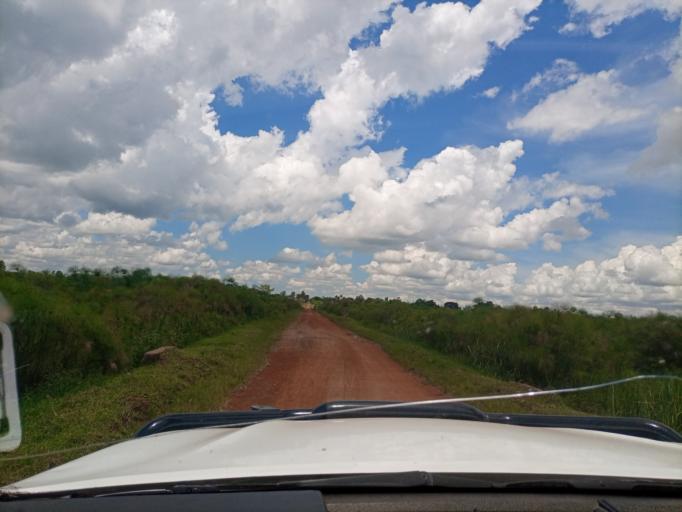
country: UG
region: Eastern Region
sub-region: Tororo District
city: Tororo
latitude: 0.6370
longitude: 33.9930
